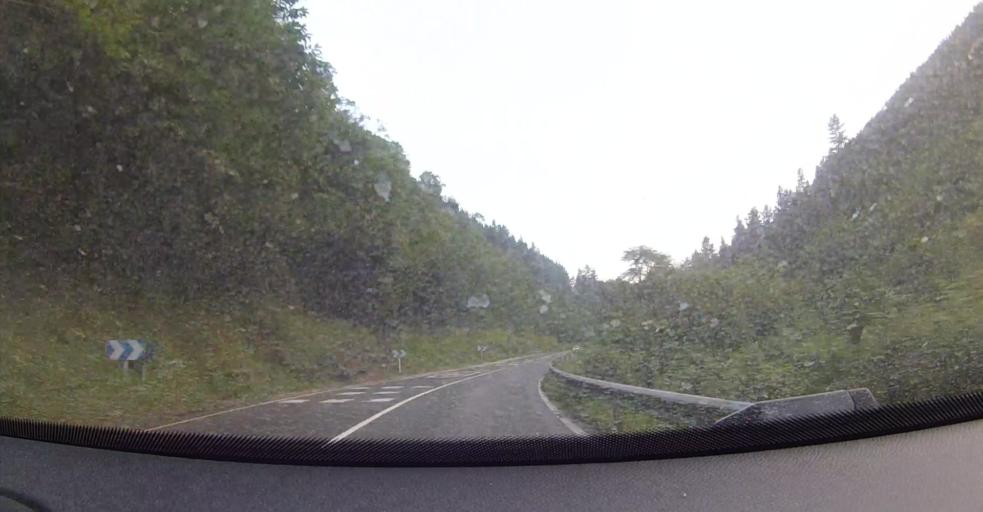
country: ES
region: Basque Country
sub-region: Bizkaia
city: Urrestieta
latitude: 43.2449
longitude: -3.1538
